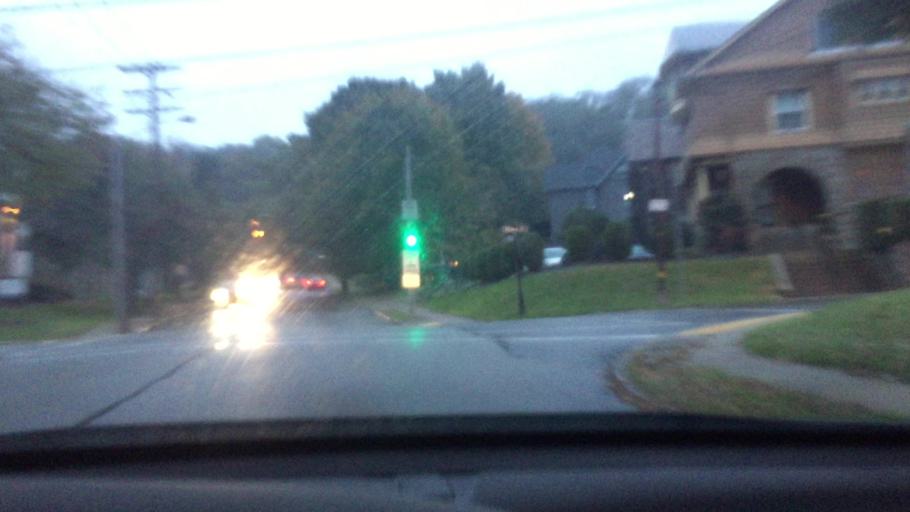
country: US
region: Pennsylvania
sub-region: Allegheny County
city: Crafton
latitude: 40.4386
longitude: -80.0636
